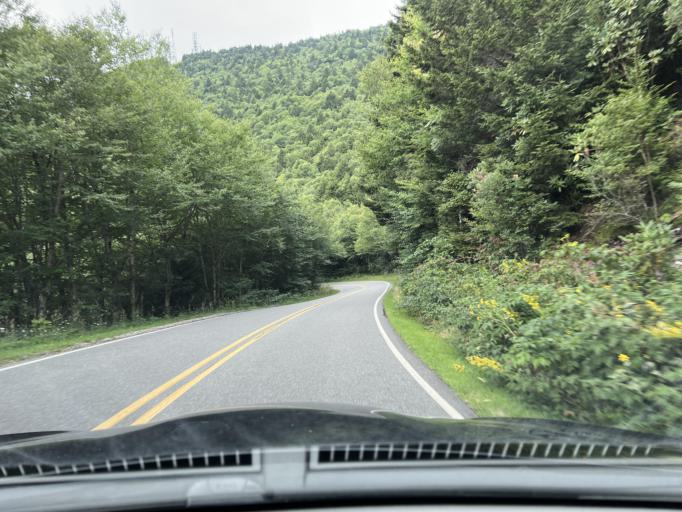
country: US
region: North Carolina
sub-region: Buncombe County
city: Black Mountain
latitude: 35.7382
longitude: -82.2799
